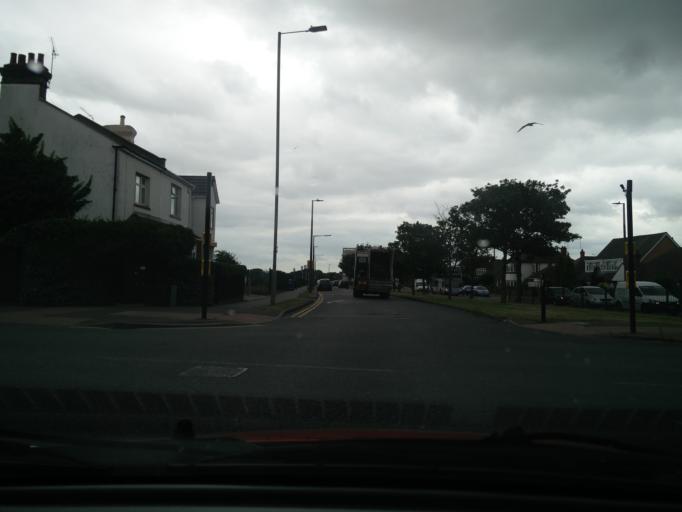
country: GB
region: England
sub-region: Southend-on-Sea
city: Westcliff-on-Sea
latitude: 51.5527
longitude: 0.6936
